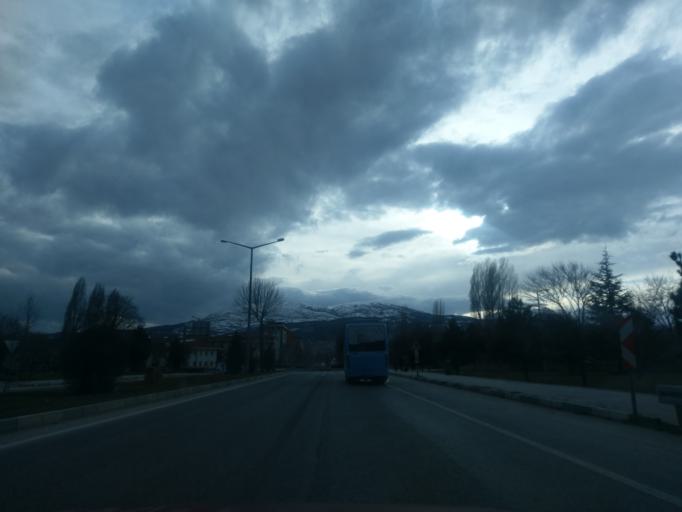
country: TR
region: Kuetahya
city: Kutahya
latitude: 39.4305
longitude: 29.9943
